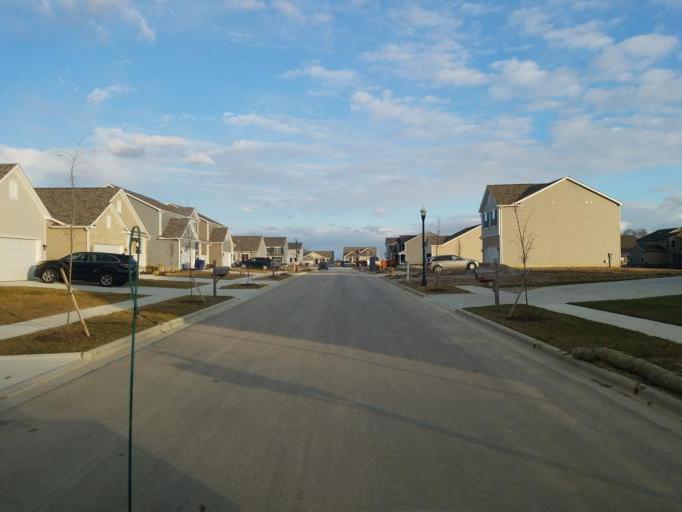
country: US
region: Ohio
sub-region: Delaware County
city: Delaware
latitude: 40.3244
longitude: -83.1145
